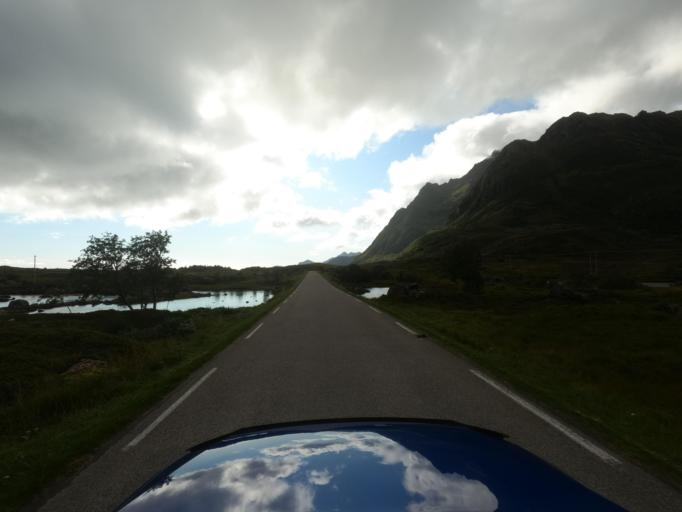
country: NO
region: Nordland
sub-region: Vestvagoy
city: Evjen
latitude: 68.1893
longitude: 13.8600
